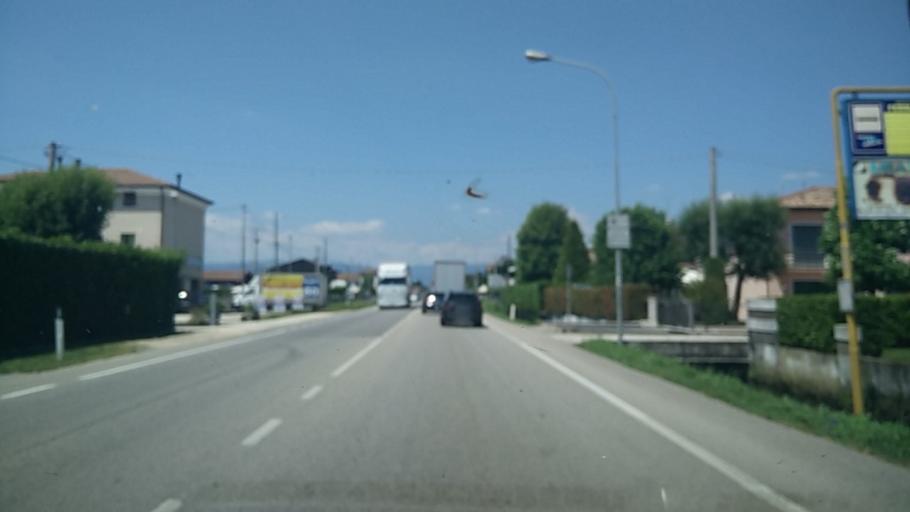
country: IT
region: Veneto
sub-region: Provincia di Padova
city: San Giorgio in Bosco
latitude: 45.6130
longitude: 11.7977
